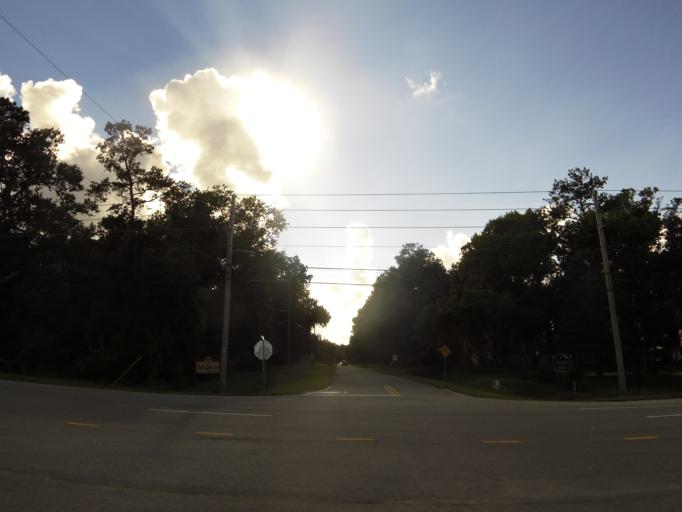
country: US
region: Georgia
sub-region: Glynn County
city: Country Club Estates
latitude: 31.2081
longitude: -81.4667
